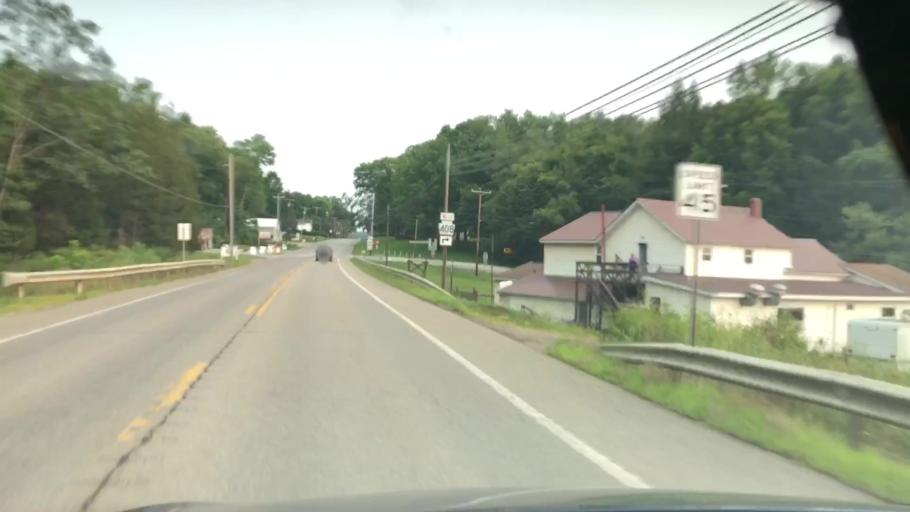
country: US
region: Pennsylvania
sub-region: Crawford County
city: Titusville
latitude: 41.6476
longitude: -79.7174
